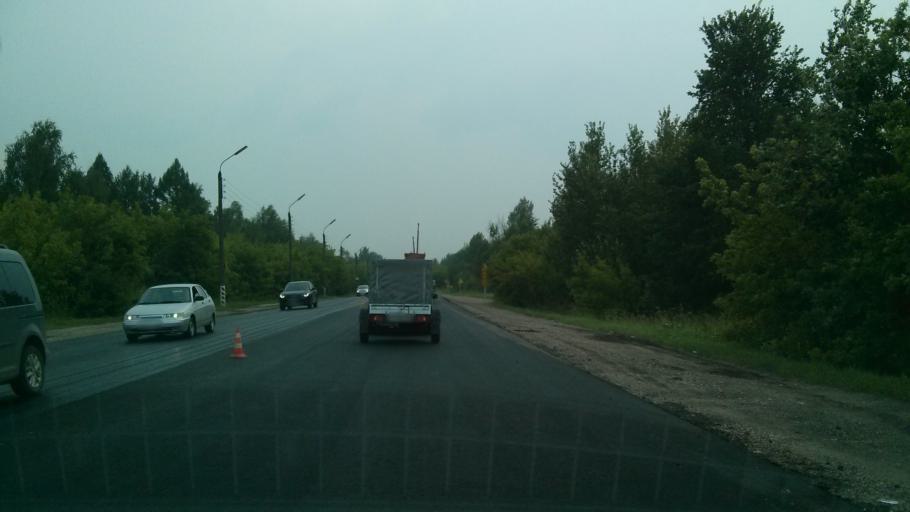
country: RU
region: Nizjnij Novgorod
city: Kstovo
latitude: 56.1133
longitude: 44.1489
